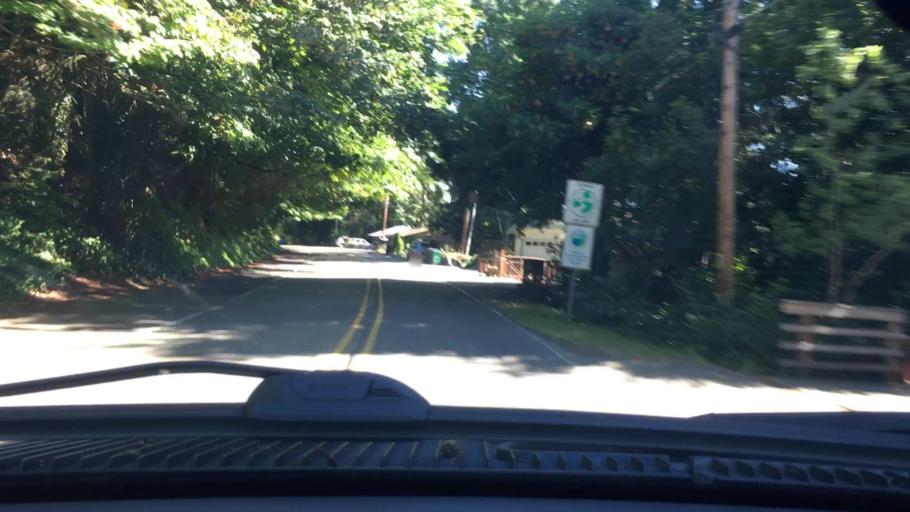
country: US
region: Washington
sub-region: King County
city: Sammamish
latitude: 47.6273
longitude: -122.0883
